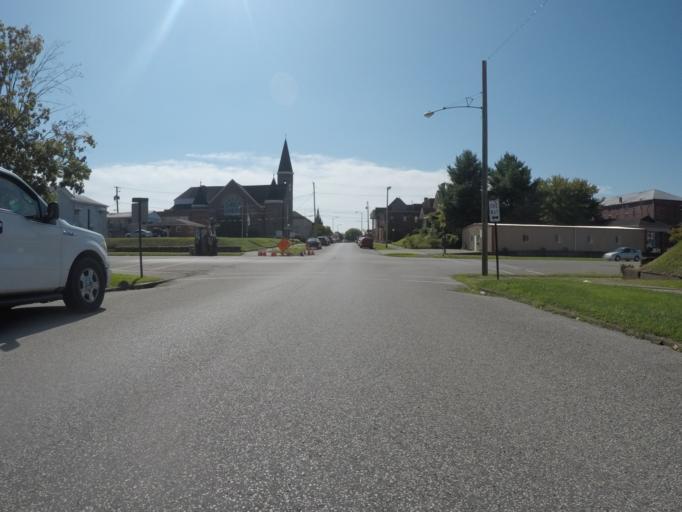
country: US
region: Ohio
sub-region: Lawrence County
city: Ironton
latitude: 38.5377
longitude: -82.6844
